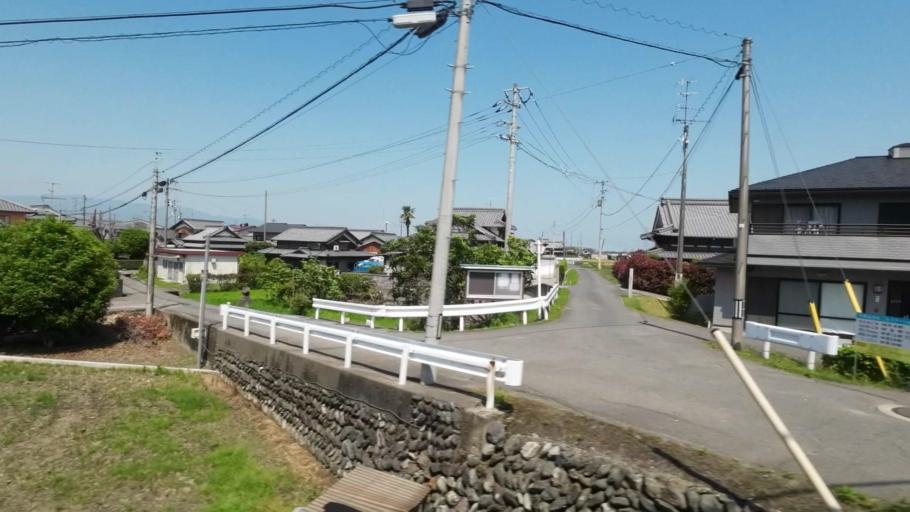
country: JP
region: Ehime
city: Saijo
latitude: 33.9022
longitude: 133.1765
